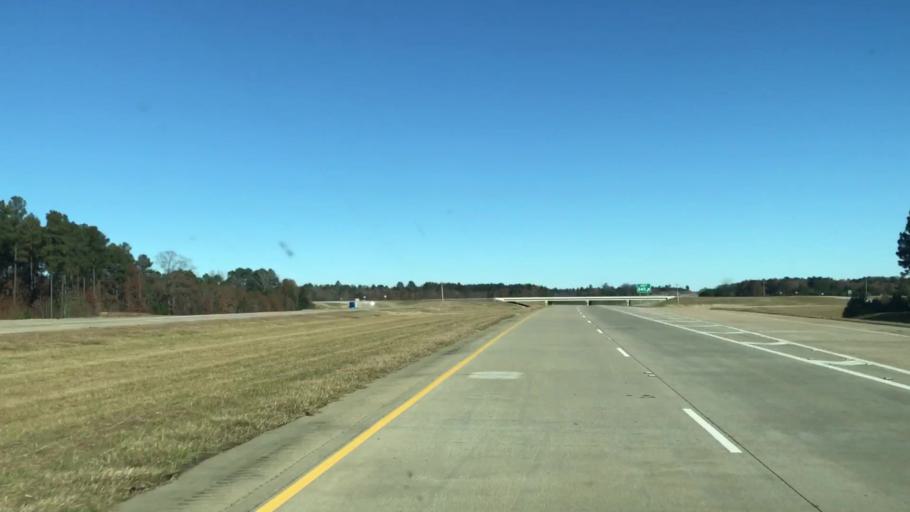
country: US
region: Louisiana
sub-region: Caddo Parish
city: Vivian
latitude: 32.9919
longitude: -93.9104
